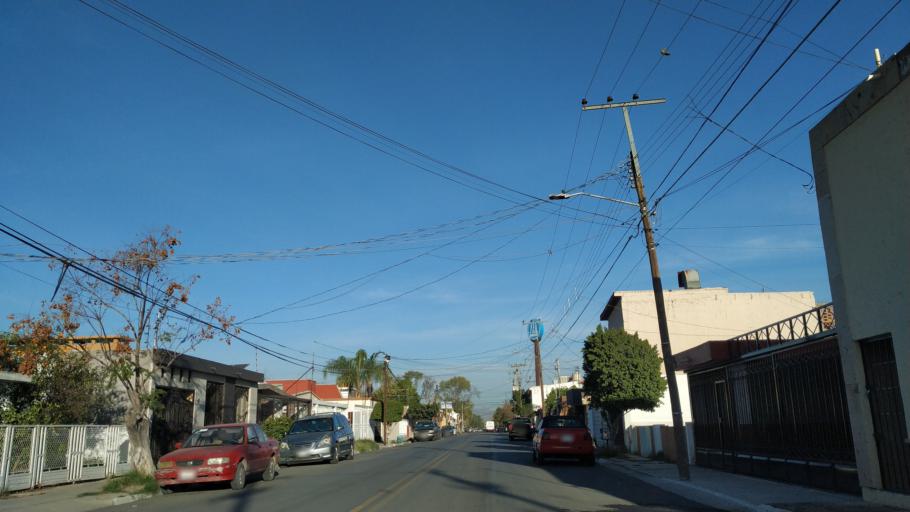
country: MX
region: Coahuila
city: Torreon
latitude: 25.5511
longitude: -103.4490
